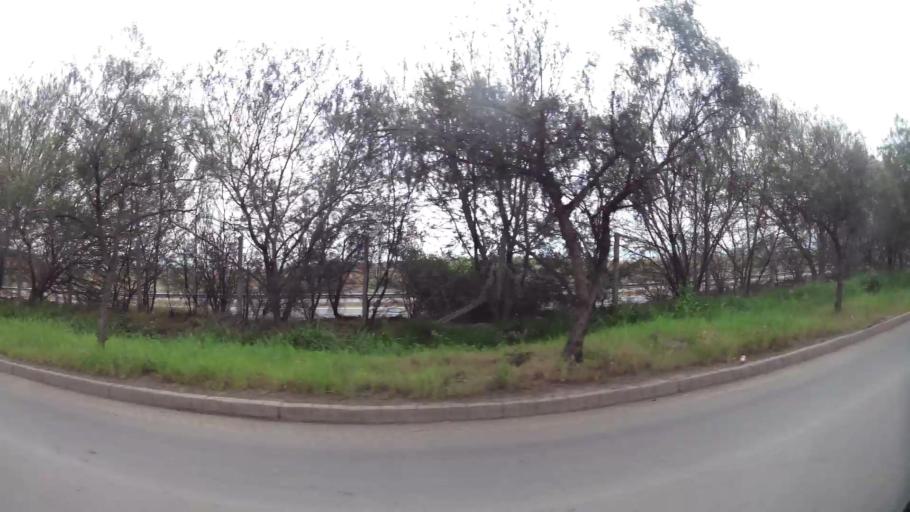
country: CL
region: Santiago Metropolitan
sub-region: Provincia de Chacabuco
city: Chicureo Abajo
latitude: -33.2006
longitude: -70.6613
